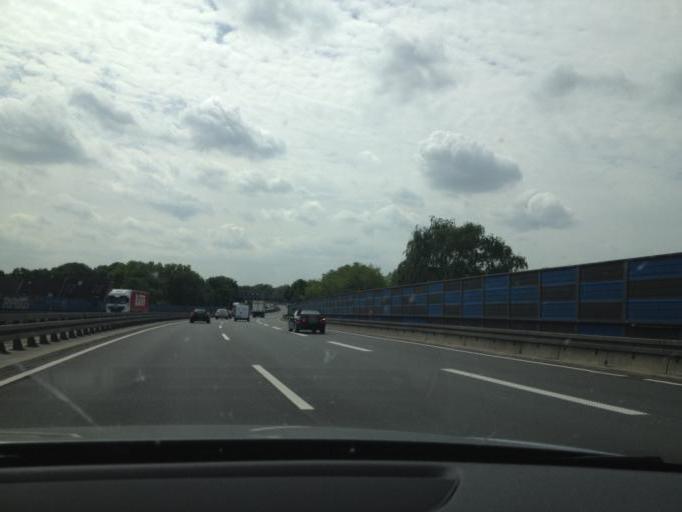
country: DE
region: North Rhine-Westphalia
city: Meiderich
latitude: 51.4673
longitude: 6.7673
